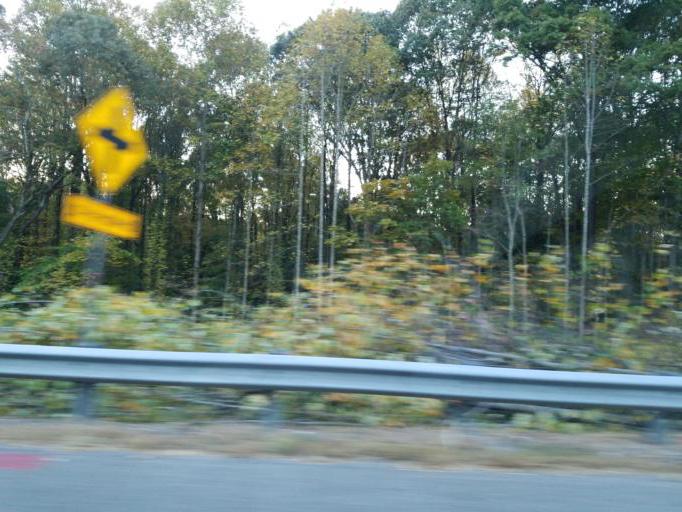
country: US
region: Georgia
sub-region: Dawson County
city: Dawsonville
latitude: 34.3306
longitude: -84.0567
